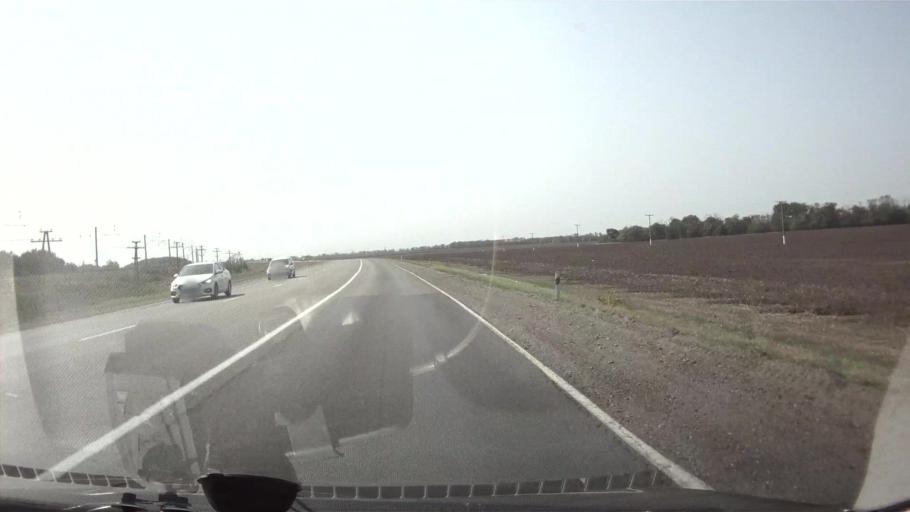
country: RU
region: Krasnodarskiy
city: Ladozhskaya
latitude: 45.3383
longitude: 39.9435
